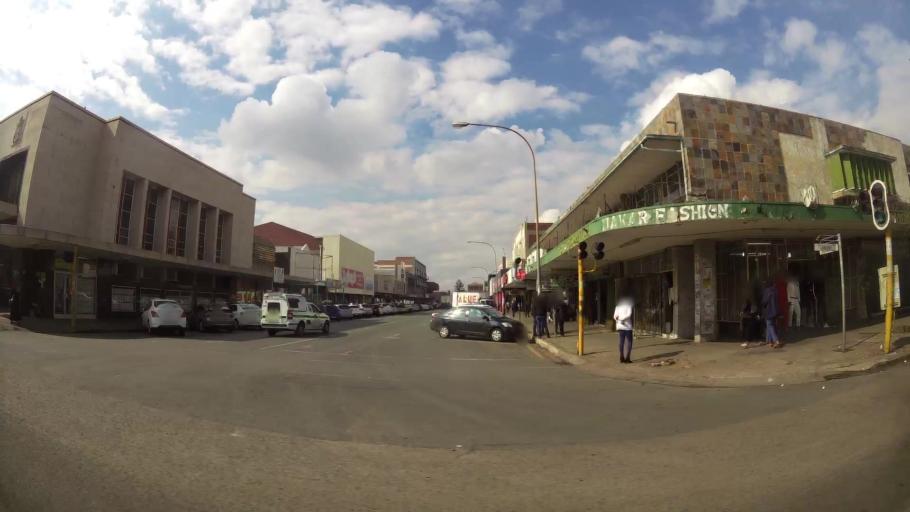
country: ZA
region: Gauteng
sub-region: Sedibeng District Municipality
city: Vereeniging
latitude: -26.6748
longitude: 27.9294
